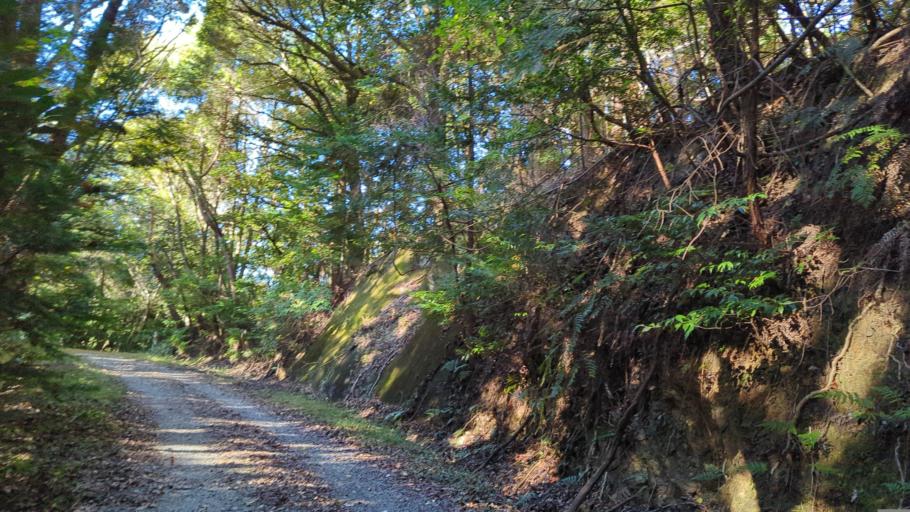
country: JP
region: Aichi
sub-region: Tokai-shi
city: Toyokawa
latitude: 34.7852
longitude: 137.4764
